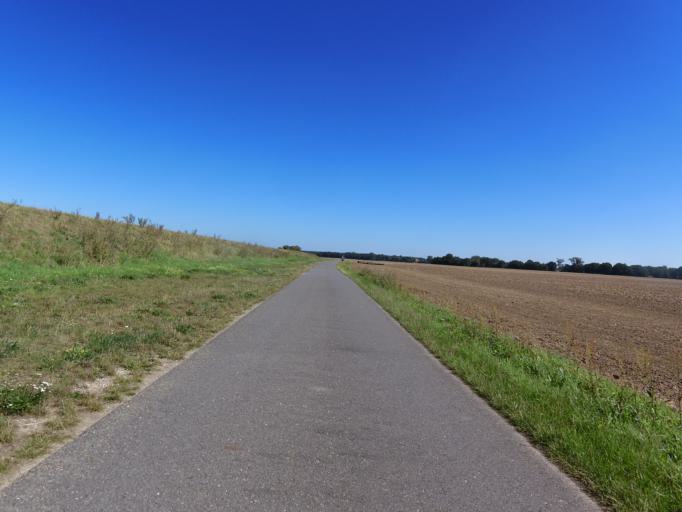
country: DE
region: Saxony-Anhalt
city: Pretzsch
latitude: 51.7356
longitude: 12.8162
